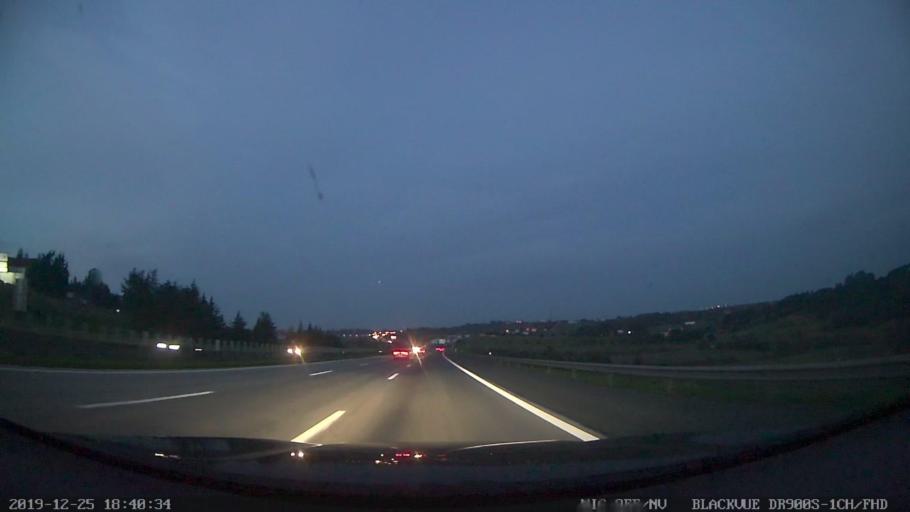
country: PT
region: Lisbon
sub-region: Azambuja
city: Aveiras de Cima
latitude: 39.1275
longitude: -8.9030
